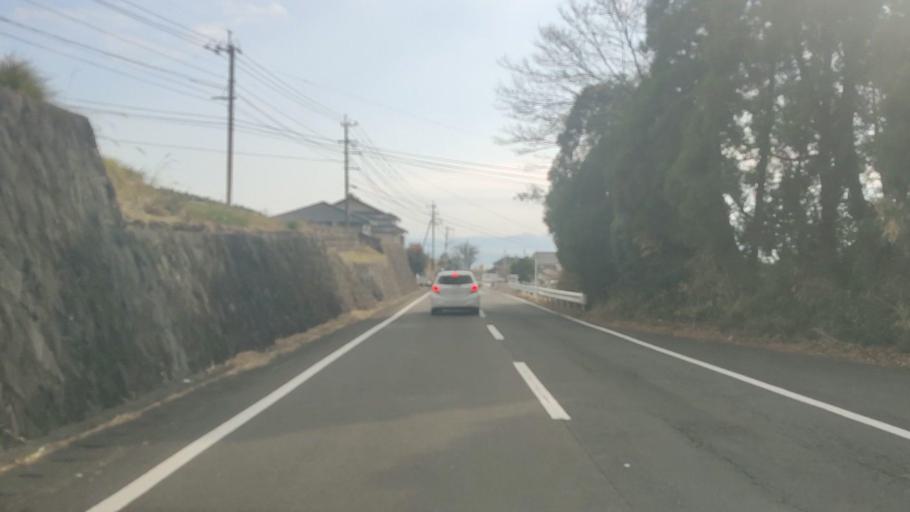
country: JP
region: Nagasaki
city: Shimabara
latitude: 32.6731
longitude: 130.2819
